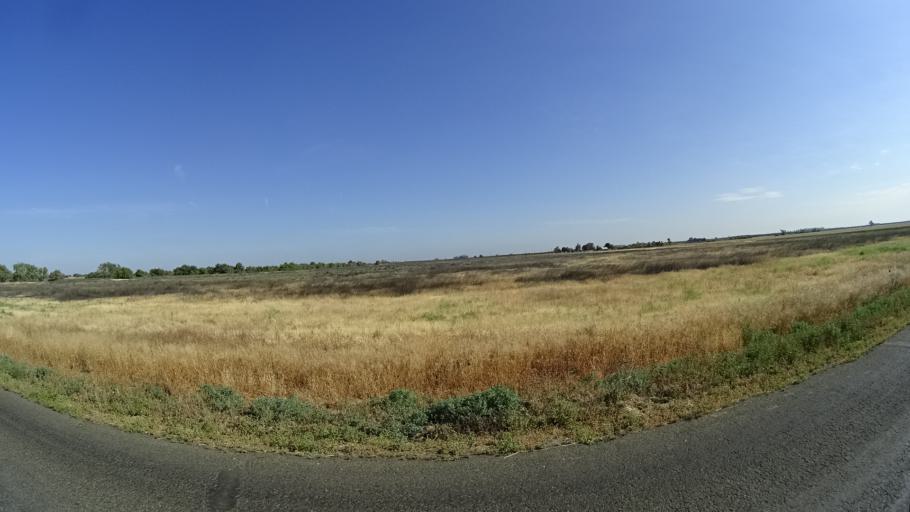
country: US
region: California
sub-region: Kings County
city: Armona
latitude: 36.2255
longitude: -119.7288
